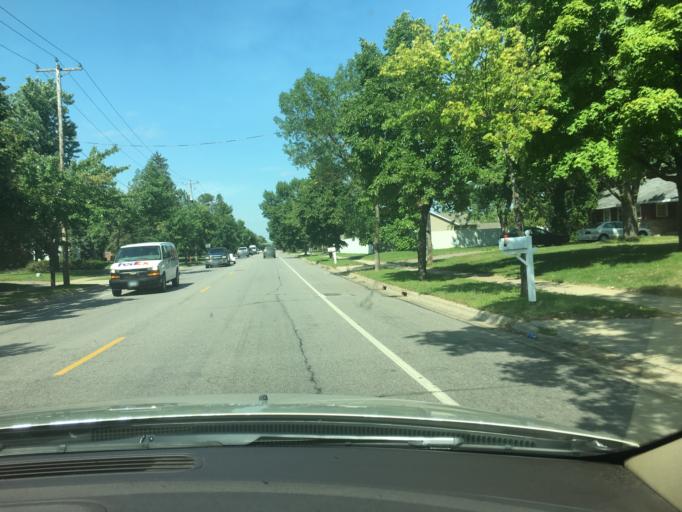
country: US
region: Minnesota
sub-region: Stearns County
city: Saint Cloud
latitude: 45.5386
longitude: -94.1618
